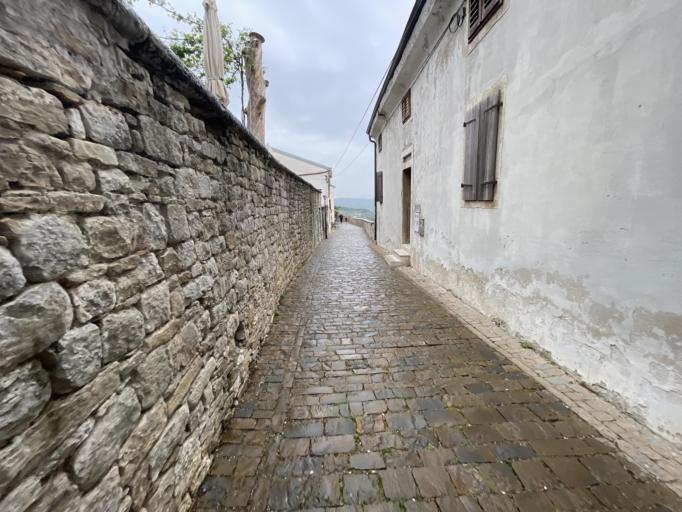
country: HR
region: Istarska
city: Karojba
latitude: 45.3364
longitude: 13.8282
